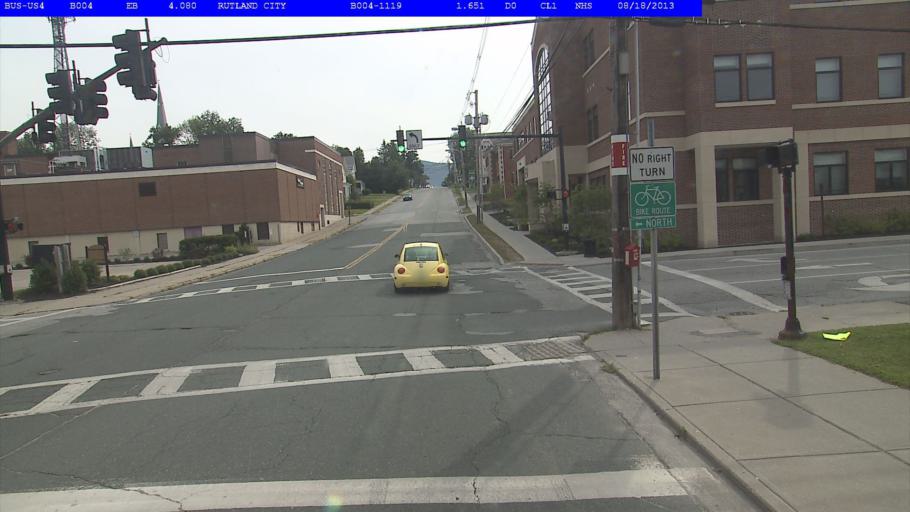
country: US
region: Vermont
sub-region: Rutland County
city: Rutland
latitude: 43.6080
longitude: -72.9780
